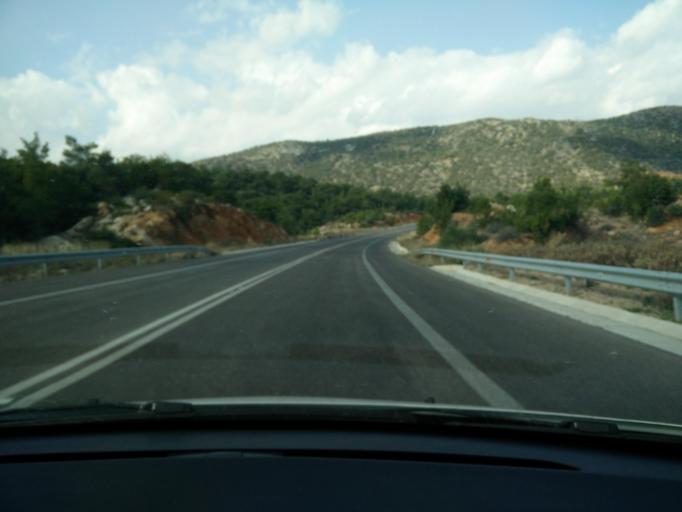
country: GR
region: Crete
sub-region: Nomos Lasithiou
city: Agios Nikolaos
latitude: 35.1413
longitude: 25.7081
